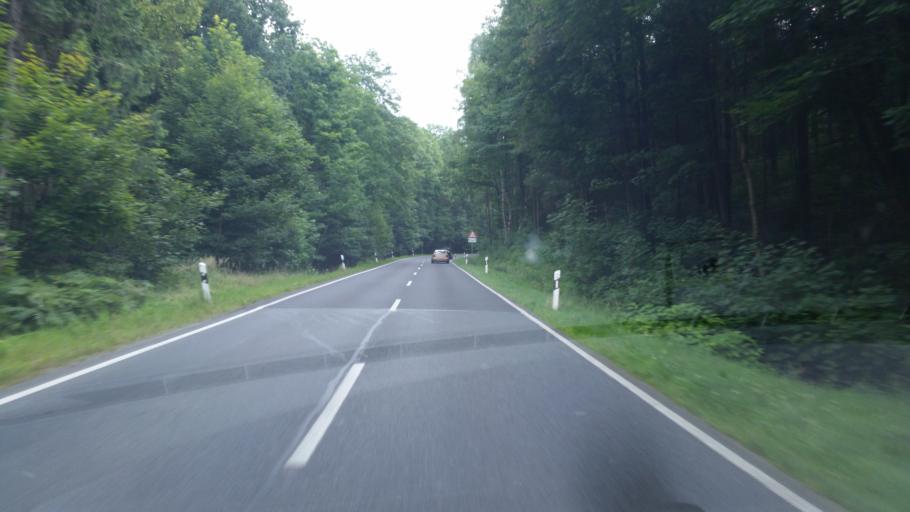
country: DE
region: Saxony
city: Neustadt in Sachsen
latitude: 51.0032
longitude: 14.2340
